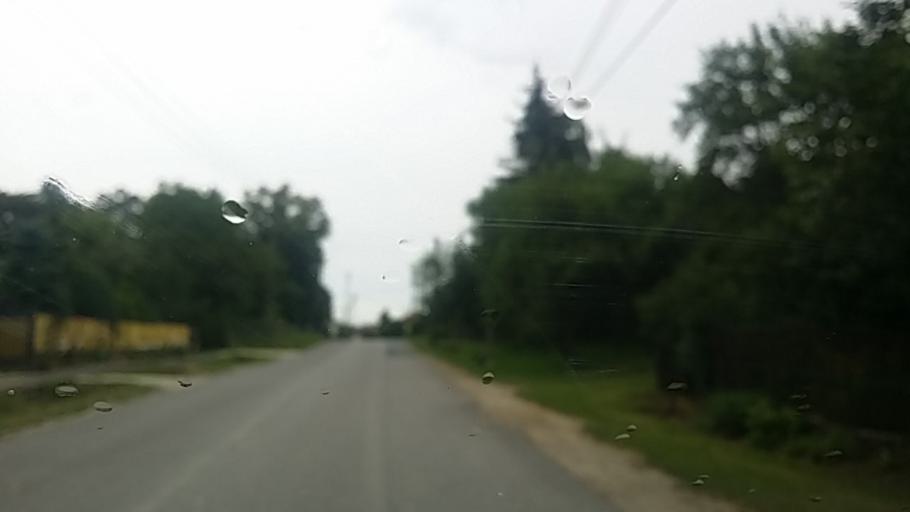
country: HU
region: Zala
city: Zalalovo
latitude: 46.8567
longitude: 16.5013
